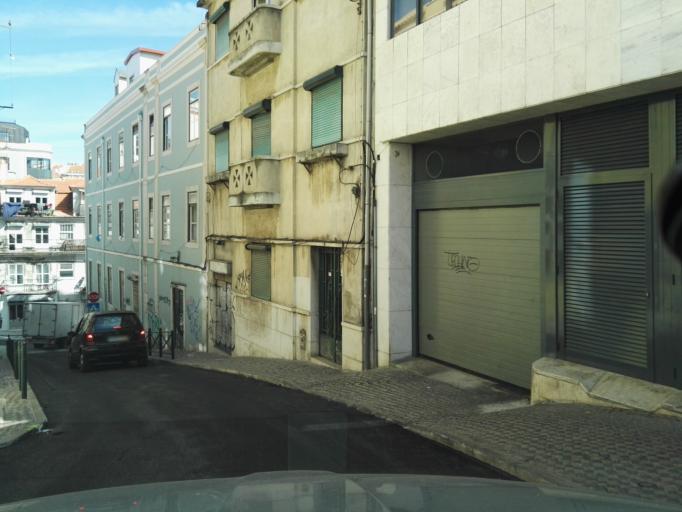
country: PT
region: Lisbon
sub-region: Lisbon
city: Lisbon
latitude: 38.7233
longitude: -9.1362
